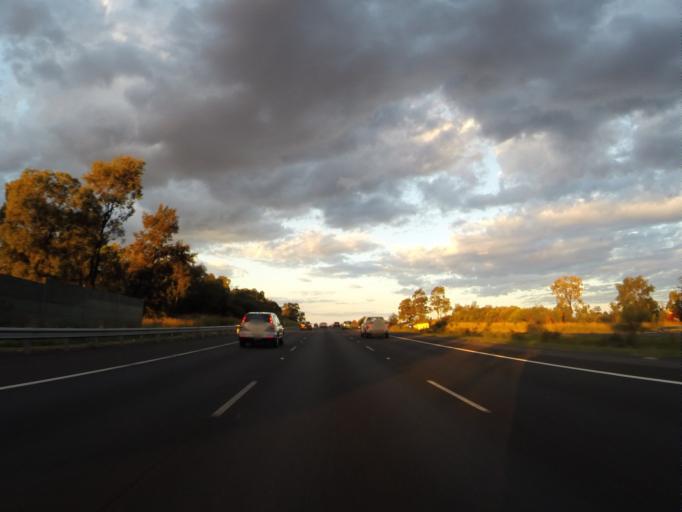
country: AU
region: New South Wales
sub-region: Campbelltown Municipality
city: Campbelltown
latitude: -34.0539
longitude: 150.8052
